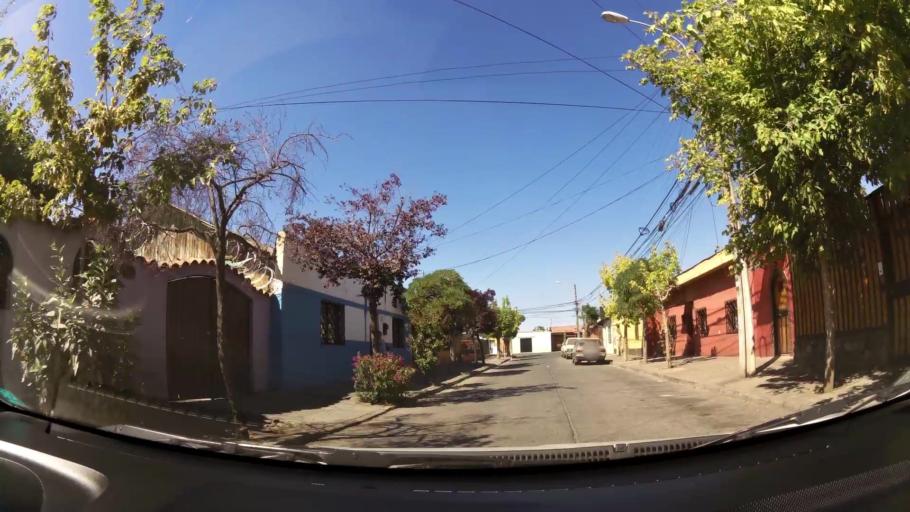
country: CL
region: O'Higgins
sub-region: Provincia de Cachapoal
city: Rancagua
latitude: -34.1798
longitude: -70.7504
